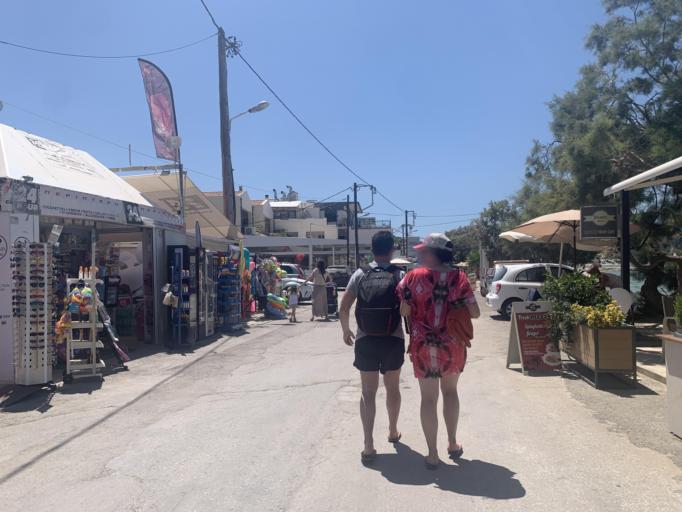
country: GR
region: Crete
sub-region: Nomos Chanias
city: Kalivai
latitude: 35.4492
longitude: 24.2024
